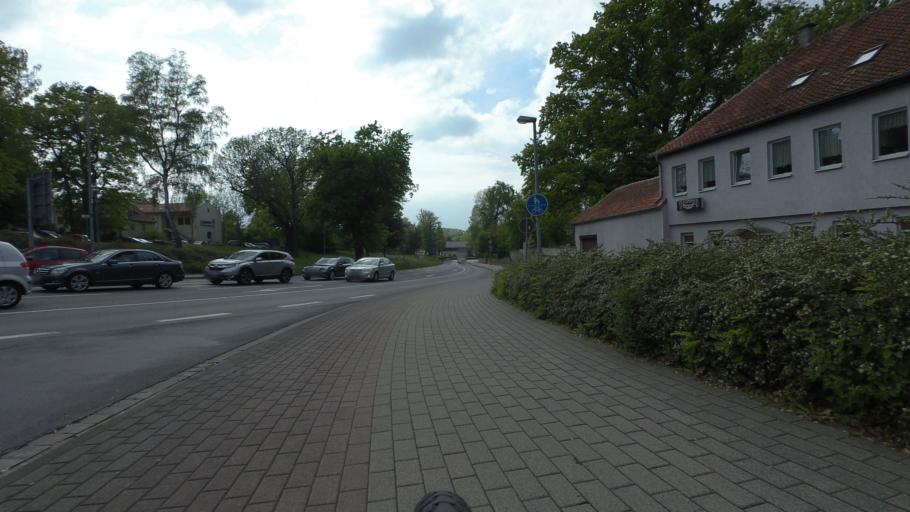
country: DE
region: Saxony-Anhalt
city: Halberstadt
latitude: 51.8935
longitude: 11.0395
